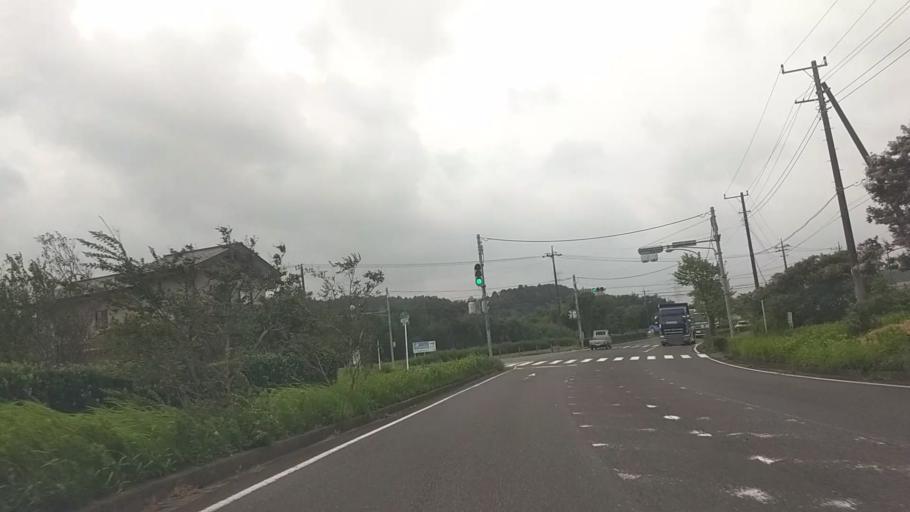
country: JP
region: Chiba
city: Kisarazu
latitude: 35.3750
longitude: 140.0126
